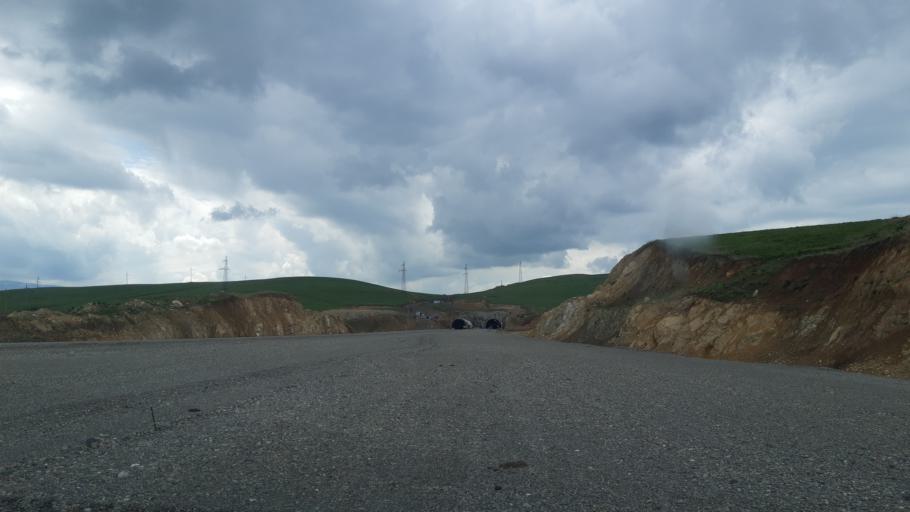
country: KZ
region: Ongtustik Qazaqstan
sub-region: Tulkibas Audany
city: Zhabagly
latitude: 42.5225
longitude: 70.5824
